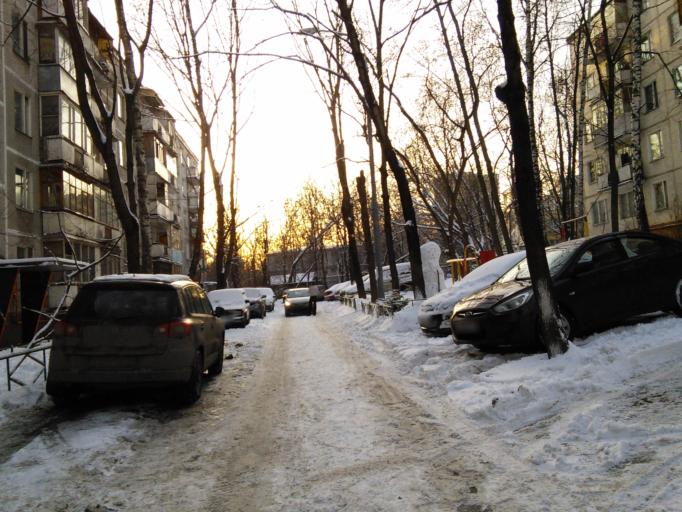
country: RU
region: Moscow
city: Davydkovo
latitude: 55.7223
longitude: 37.4733
